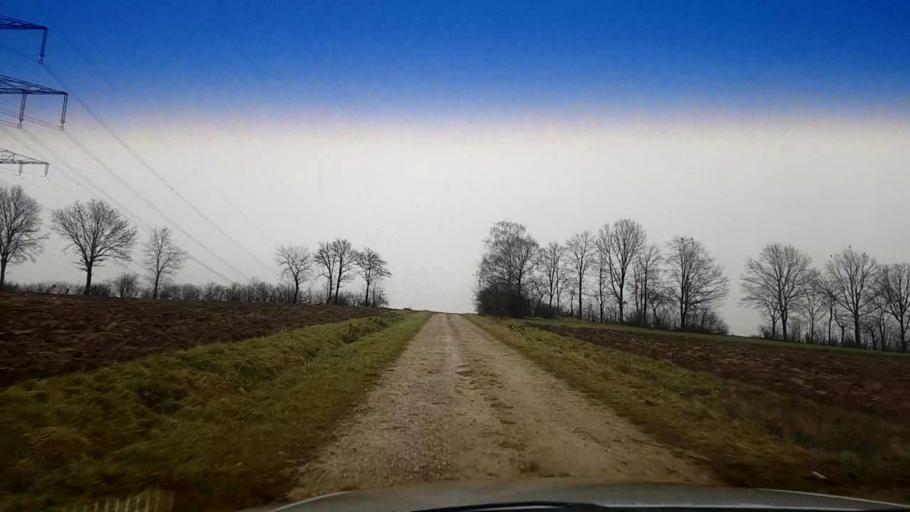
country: DE
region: Bavaria
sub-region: Upper Franconia
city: Memmelsdorf
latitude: 49.9578
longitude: 10.9784
